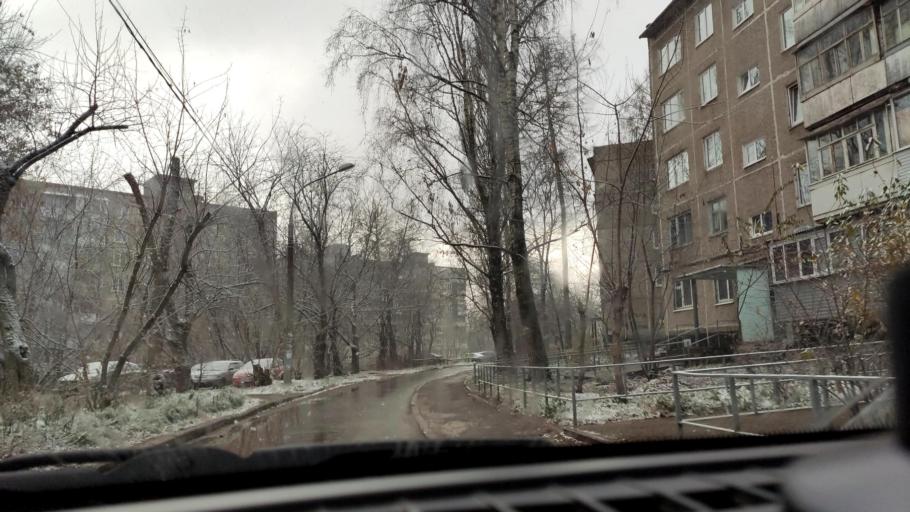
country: RU
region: Perm
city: Perm
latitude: 57.9828
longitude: 56.2230
